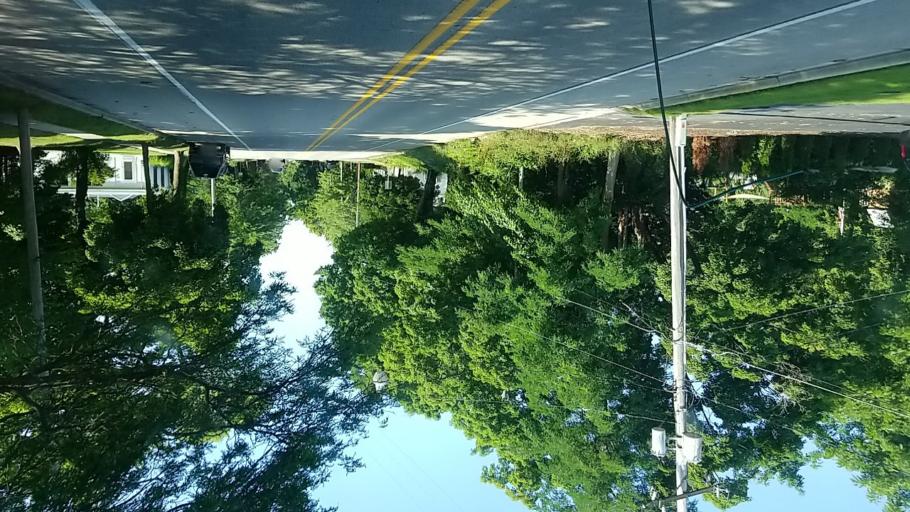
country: US
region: Michigan
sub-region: Muskegon County
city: Whitehall
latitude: 43.4005
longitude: -86.3478
